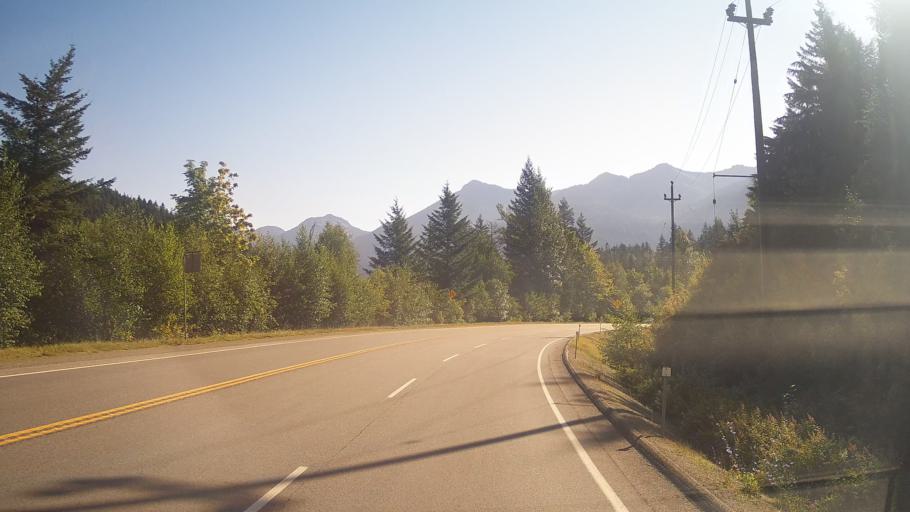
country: CA
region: British Columbia
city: Hope
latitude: 49.4082
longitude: -121.4519
